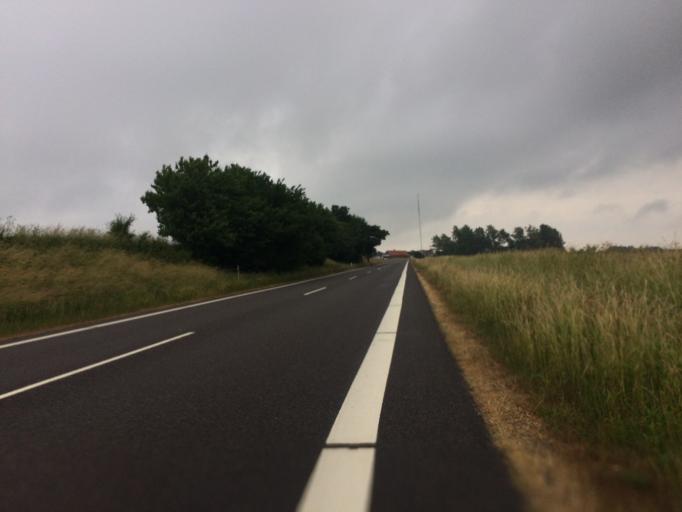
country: DK
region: Capital Region
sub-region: Bornholm Kommune
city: Akirkeby
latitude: 55.1418
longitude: 14.8636
